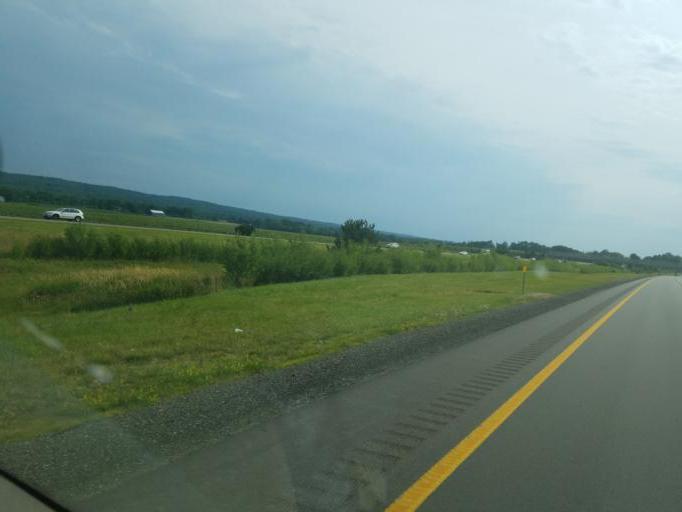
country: US
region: New York
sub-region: Chautauqua County
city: Westfield
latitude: 42.3006
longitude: -79.6538
